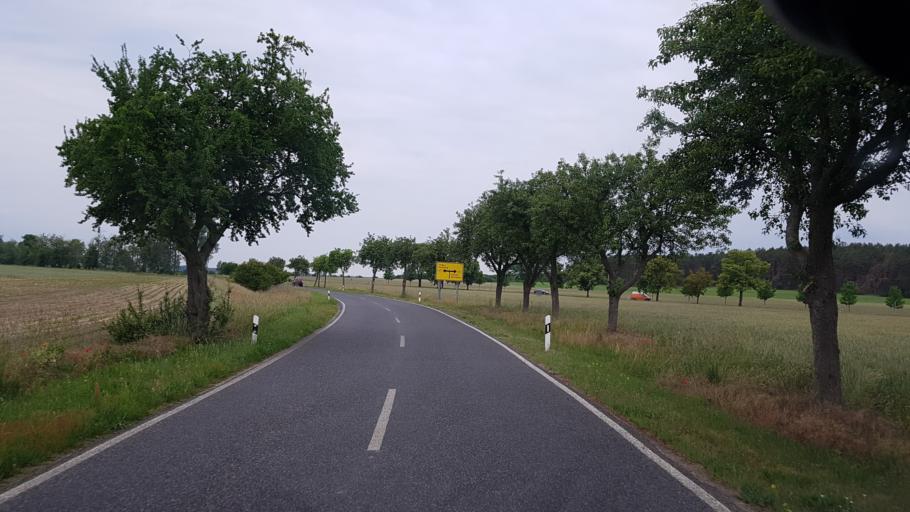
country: DE
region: Brandenburg
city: Herzberg
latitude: 51.7182
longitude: 13.2913
